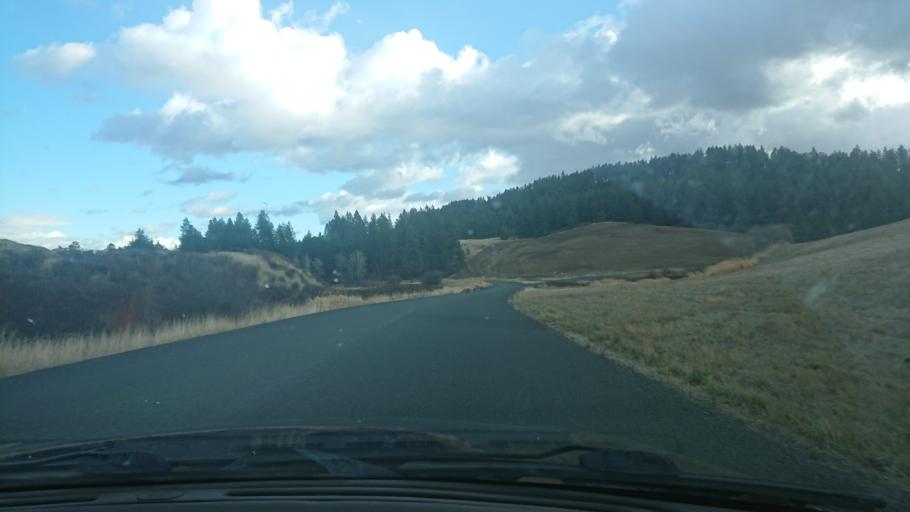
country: US
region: Idaho
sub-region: Latah County
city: Moscow
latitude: 46.7028
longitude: -116.8627
